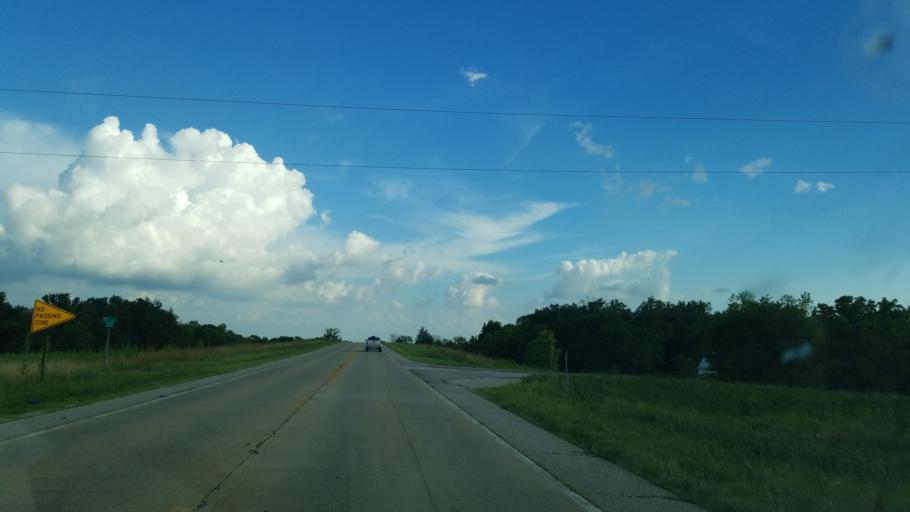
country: US
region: Illinois
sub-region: Marion County
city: Sandoval
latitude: 38.5838
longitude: -89.1084
